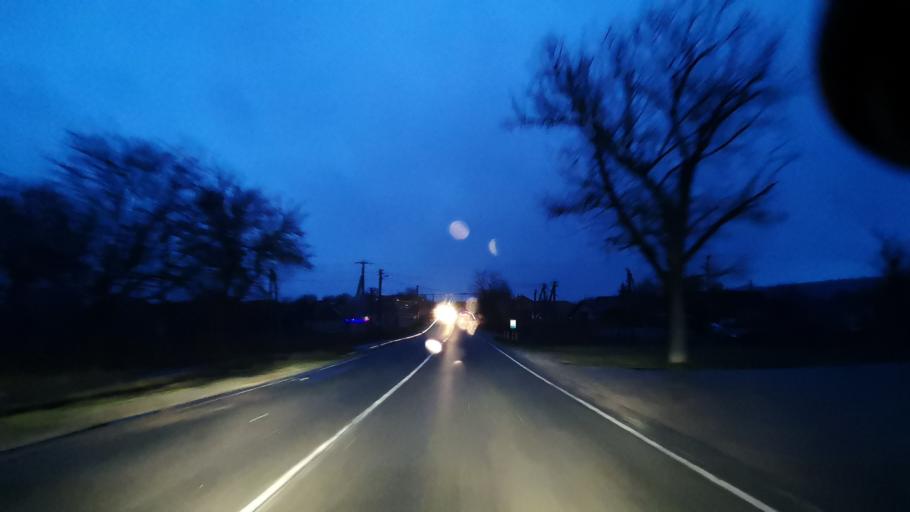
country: MD
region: Orhei
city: Orhei
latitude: 47.4599
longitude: 28.7905
